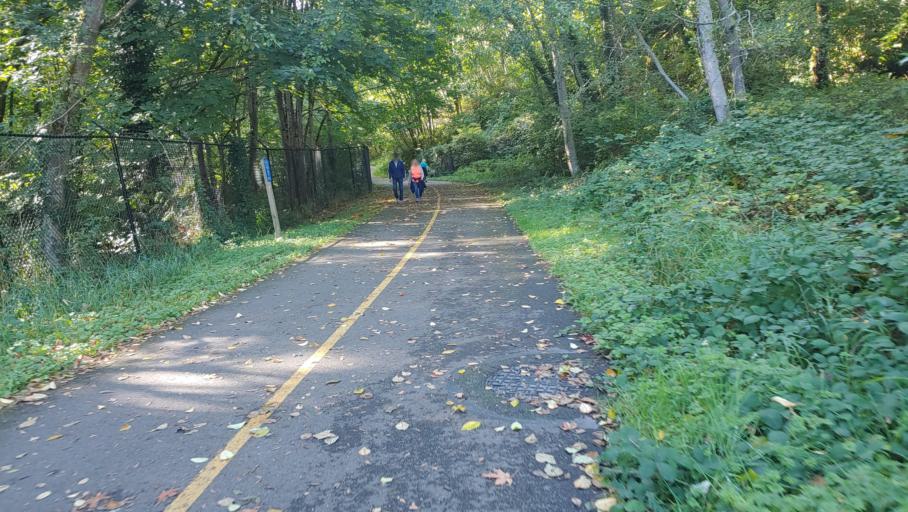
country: US
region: Washington
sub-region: King County
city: Des Moines
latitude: 47.4119
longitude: -122.3199
